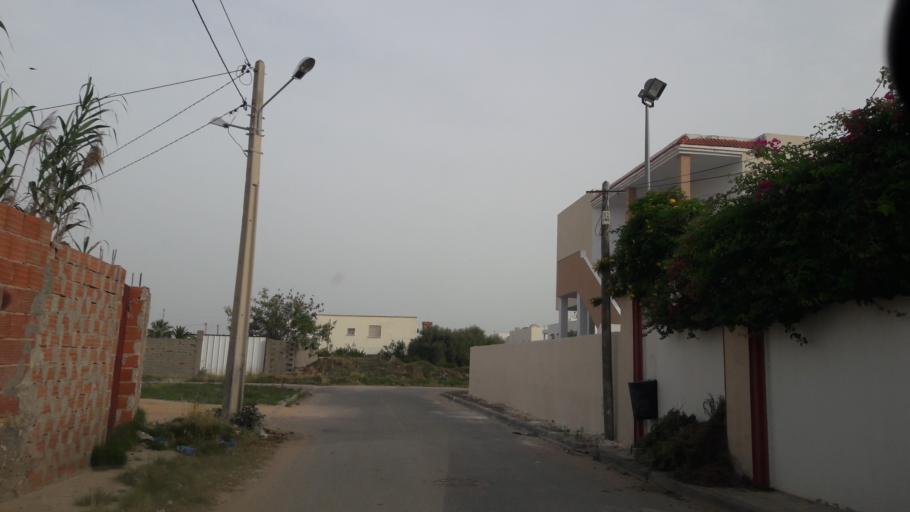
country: TN
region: Safaqis
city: Al Qarmadah
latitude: 34.7770
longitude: 10.7668
